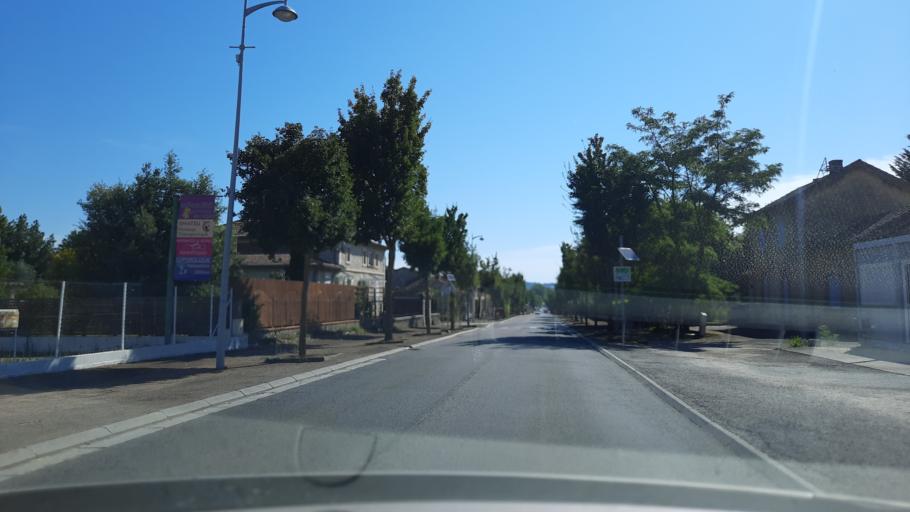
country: FR
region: Midi-Pyrenees
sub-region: Departement du Tarn-et-Garonne
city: Septfonds
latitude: 44.1756
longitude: 1.6146
